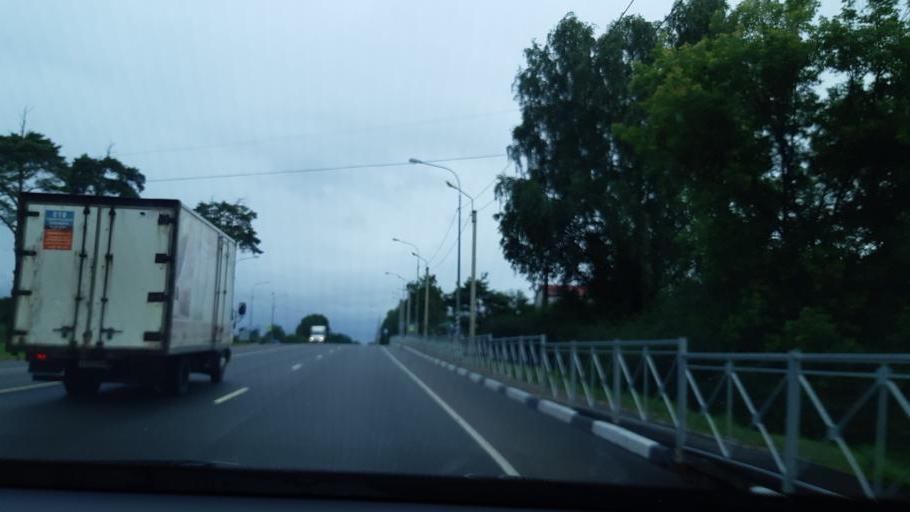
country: RU
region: Smolensk
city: Oster
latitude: 53.9872
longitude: 32.8223
